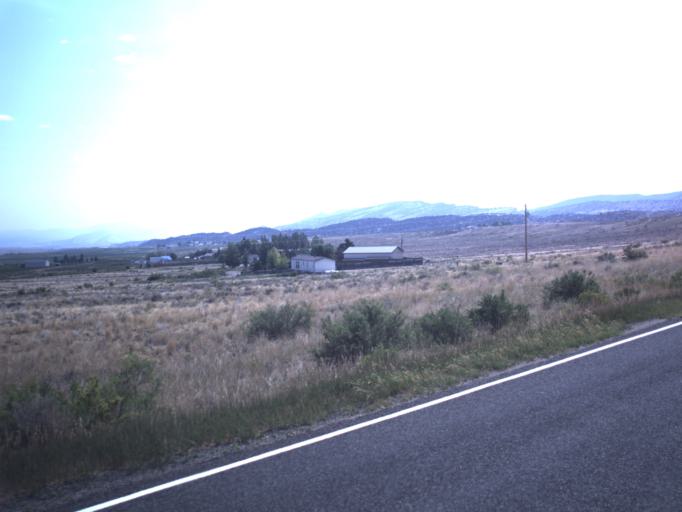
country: US
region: Utah
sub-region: Daggett County
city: Manila
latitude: 40.9724
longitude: -109.7181
